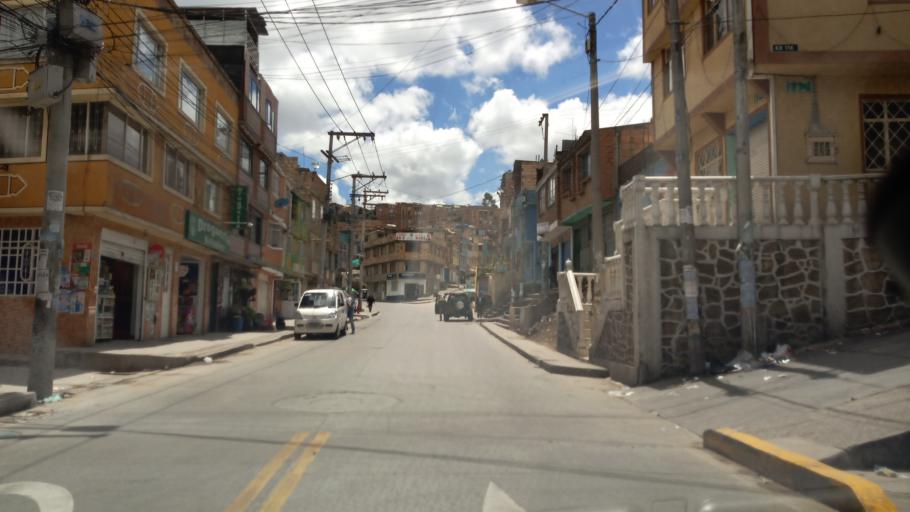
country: CO
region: Bogota D.C.
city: Bogota
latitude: 4.5666
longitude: -74.1137
